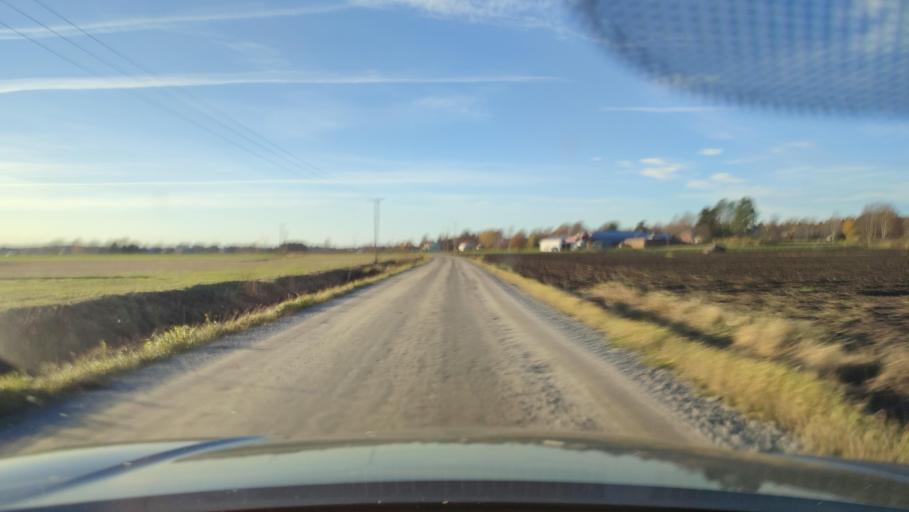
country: FI
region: Ostrobothnia
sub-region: Vaasa
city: Ristinummi
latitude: 63.0105
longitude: 21.7049
